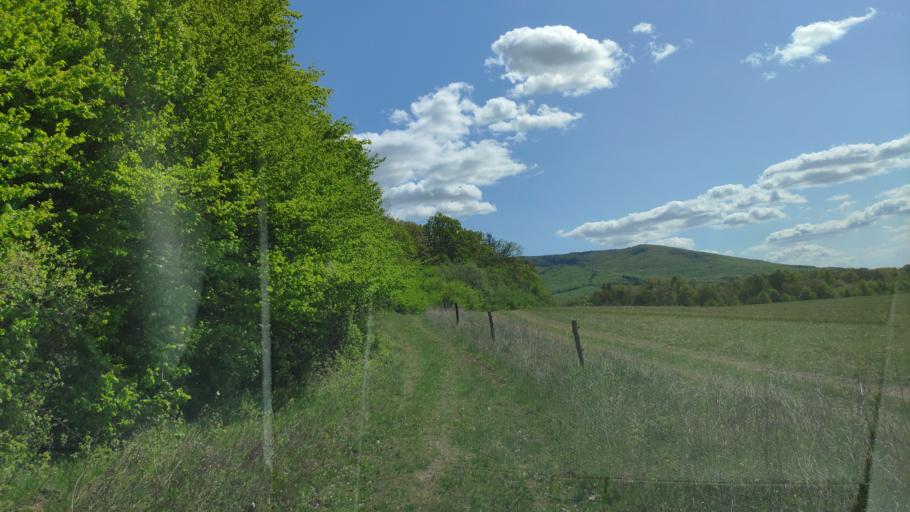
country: SK
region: Kosicky
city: Kosice
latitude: 48.6564
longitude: 21.4299
